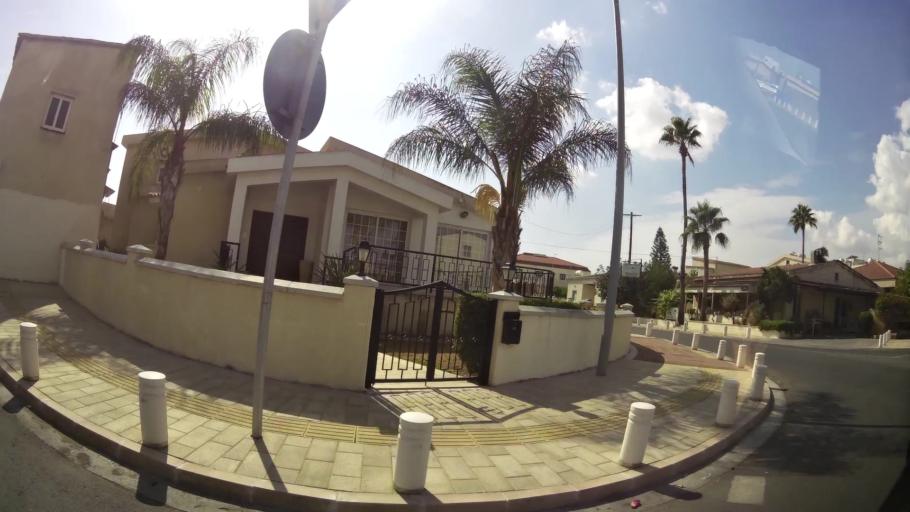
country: CY
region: Larnaka
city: Aradippou
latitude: 34.9499
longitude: 33.5934
